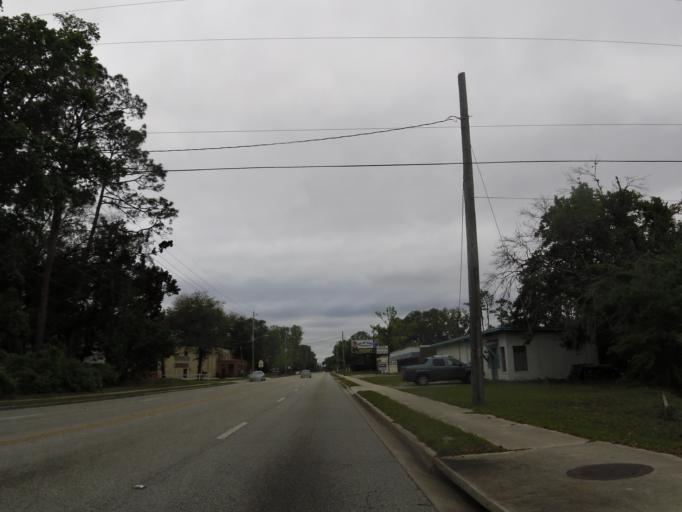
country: US
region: Florida
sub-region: Duval County
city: Jacksonville
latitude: 30.2652
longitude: -81.6312
